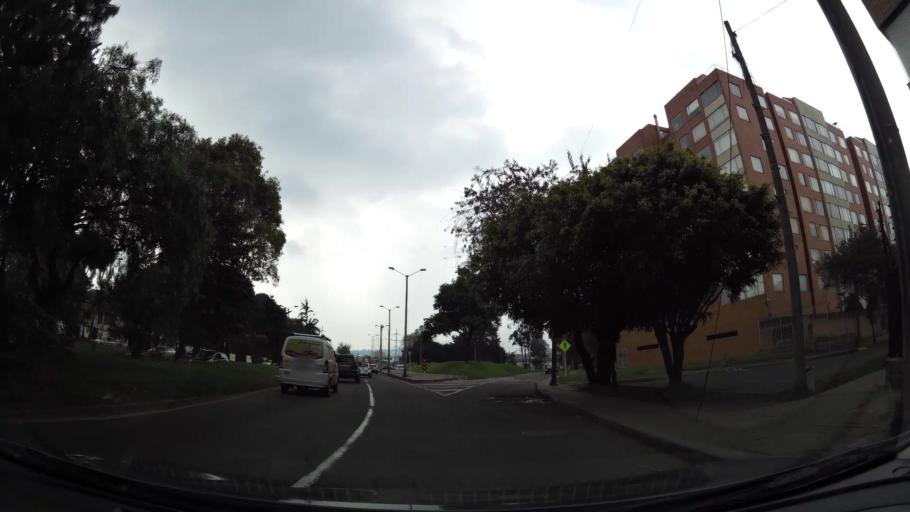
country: CO
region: Bogota D.C.
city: Barrio San Luis
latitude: 4.7187
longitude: -74.0494
